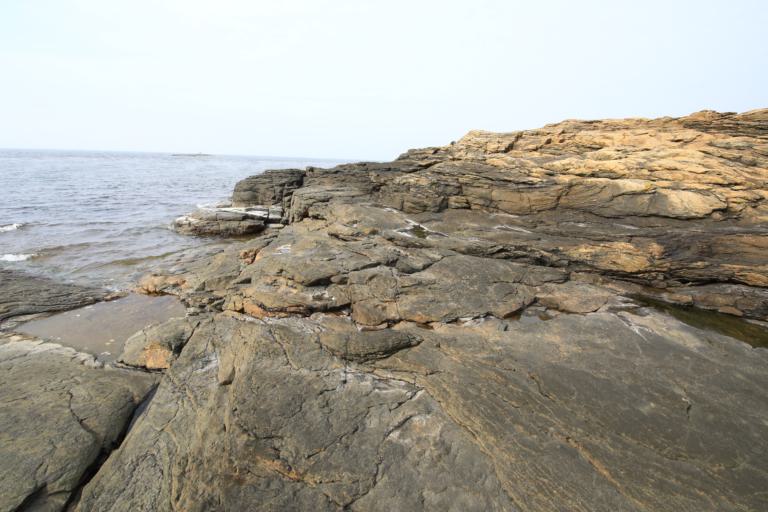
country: SE
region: Halland
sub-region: Kungsbacka Kommun
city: Frillesas
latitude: 57.2486
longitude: 12.0913
